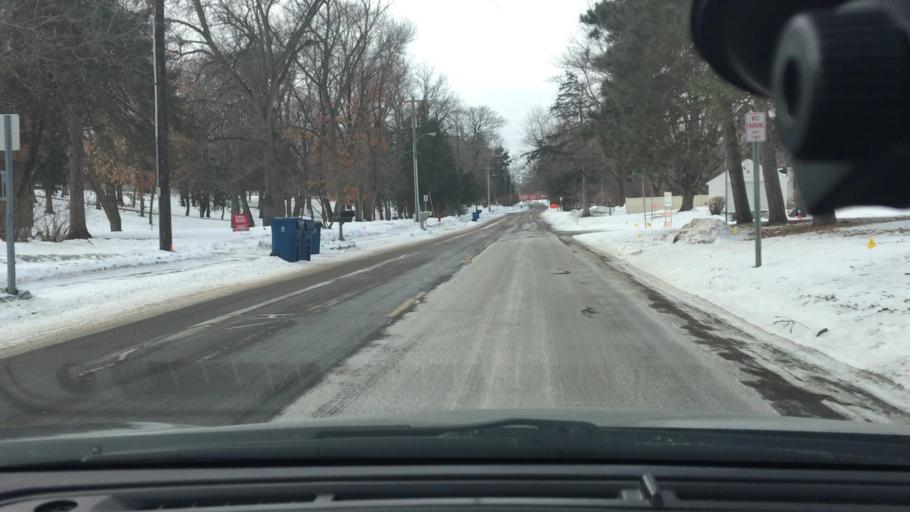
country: US
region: Minnesota
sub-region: Hennepin County
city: Champlin
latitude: 45.1859
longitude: -93.3948
